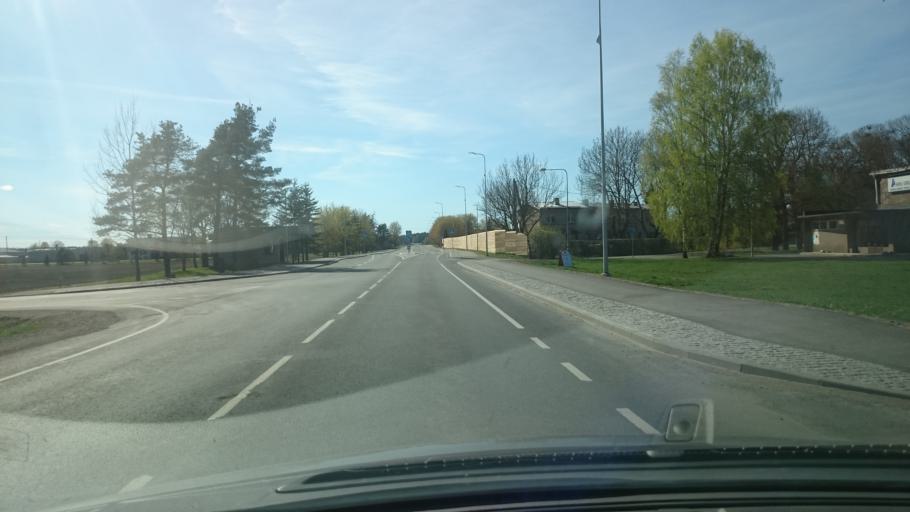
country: EE
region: Laeaene-Virumaa
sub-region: Kadrina vald
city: Kadrina
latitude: 59.3517
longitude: 26.2190
